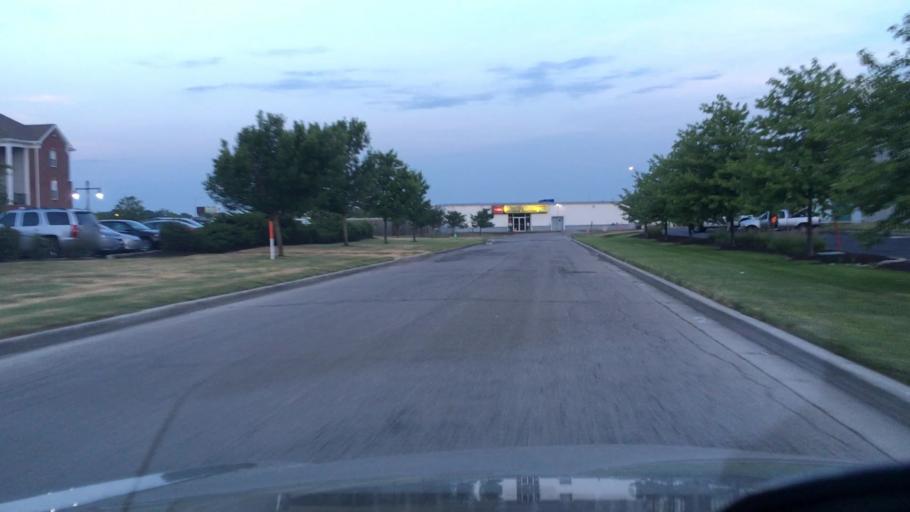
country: US
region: Indiana
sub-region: Marion County
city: Lawrence
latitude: 39.8943
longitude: -86.0493
